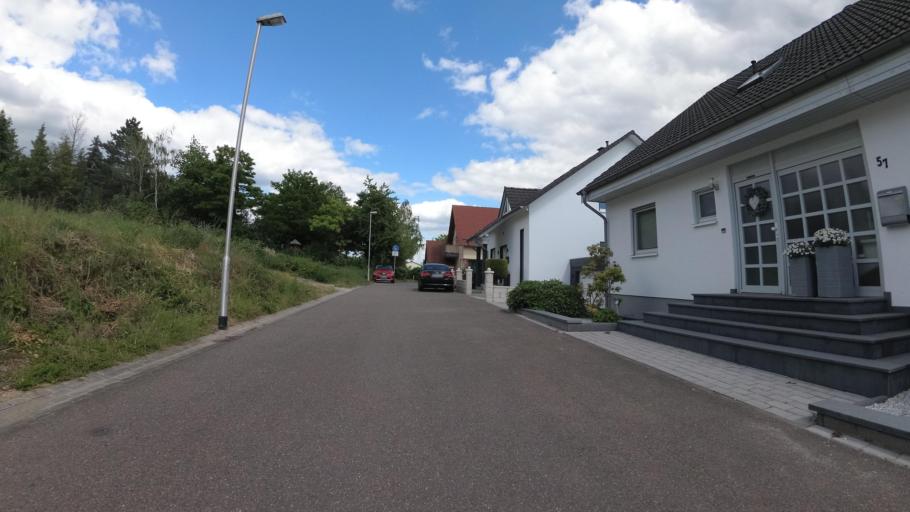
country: DE
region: Saarland
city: Volklingen
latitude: 49.2609
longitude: 6.8630
